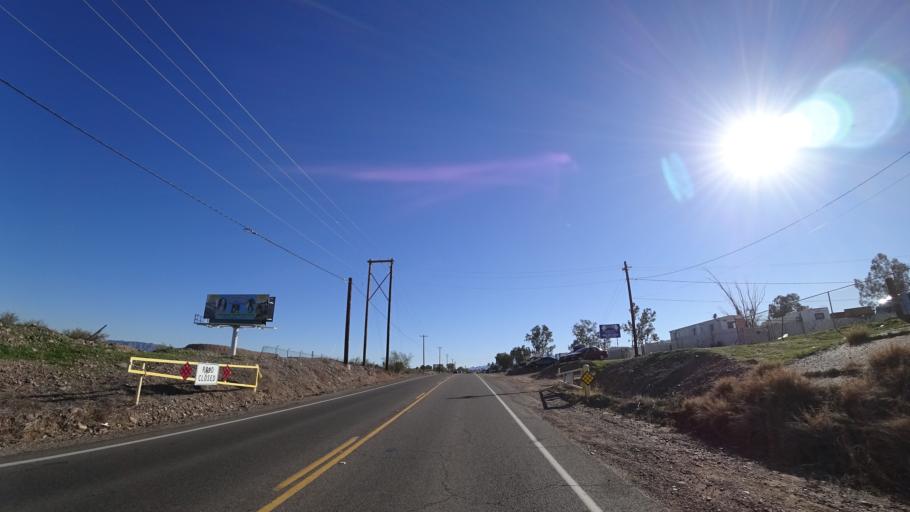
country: US
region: Arizona
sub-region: Maricopa County
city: Laveen
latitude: 33.3953
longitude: -112.2033
